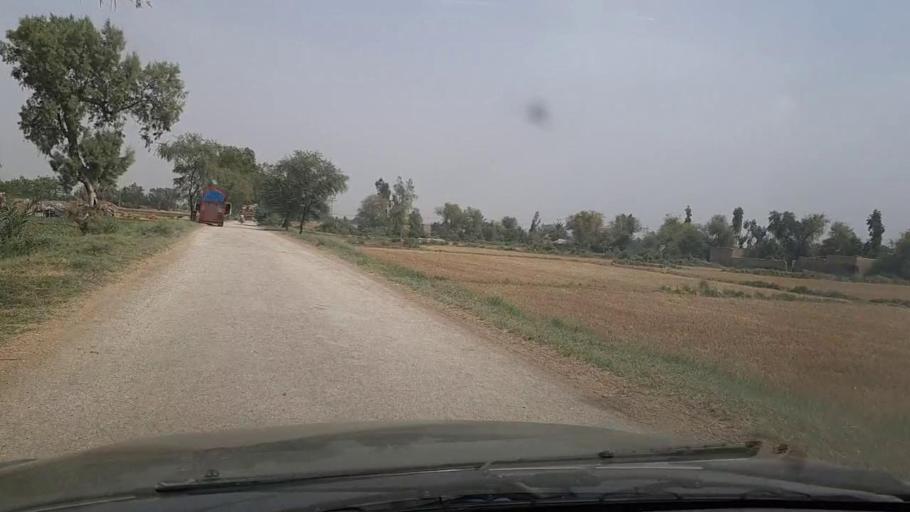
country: PK
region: Sindh
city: Shikarpur
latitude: 27.9198
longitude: 68.6791
